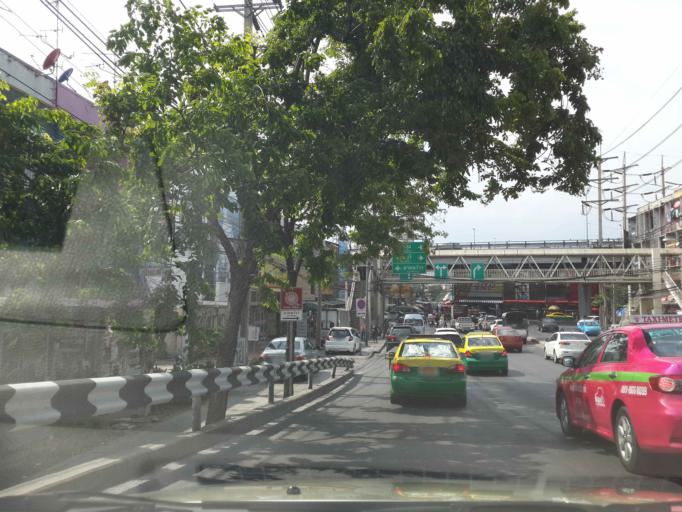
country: TH
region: Bangkok
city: Bang Kapi
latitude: 13.7654
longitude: 100.6454
